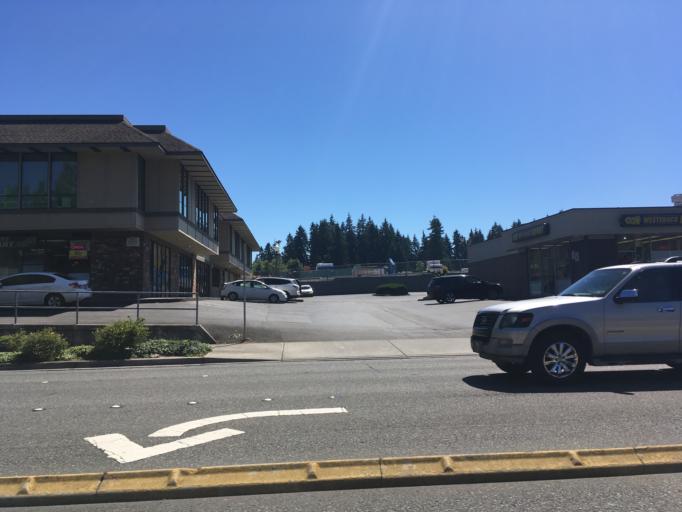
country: US
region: Washington
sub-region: King County
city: Eastgate
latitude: 47.6230
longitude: -122.1325
